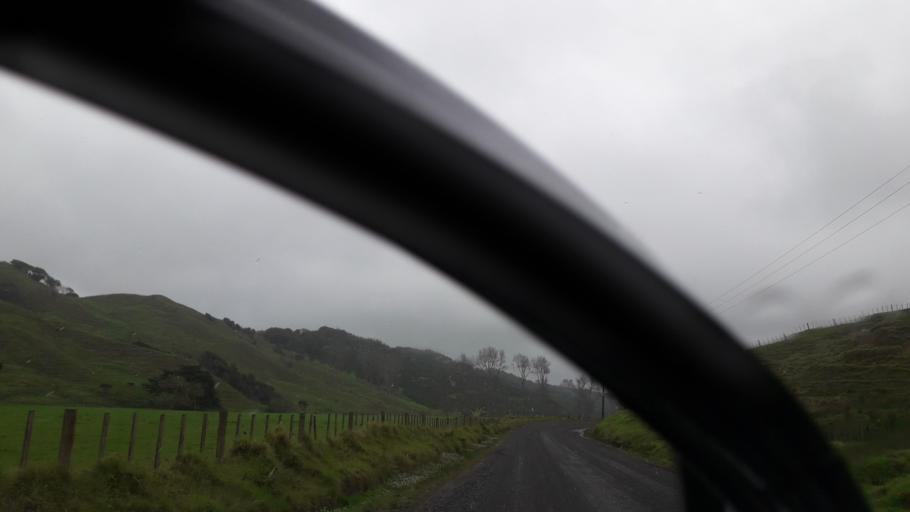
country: NZ
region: Northland
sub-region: Far North District
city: Ahipara
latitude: -35.4224
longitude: 173.3599
